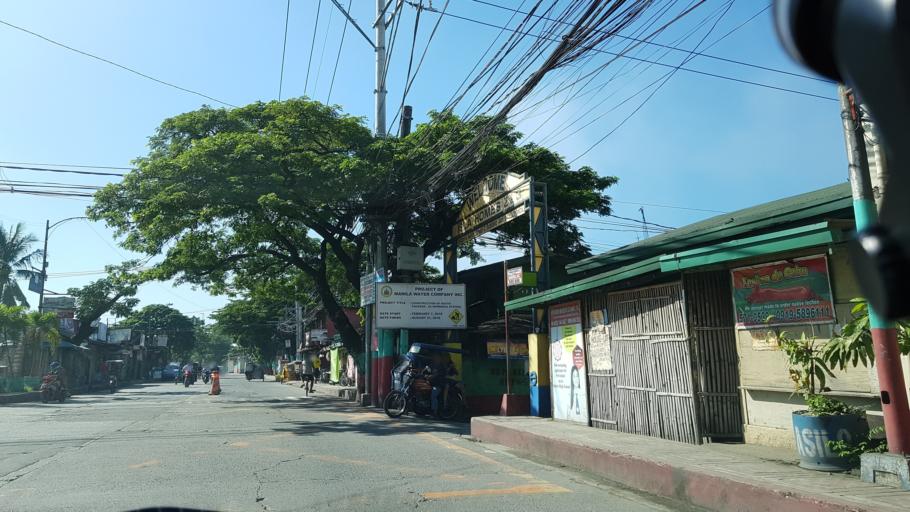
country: PH
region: Calabarzon
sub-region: Province of Rizal
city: Pateros
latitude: 14.5615
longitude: 121.0942
